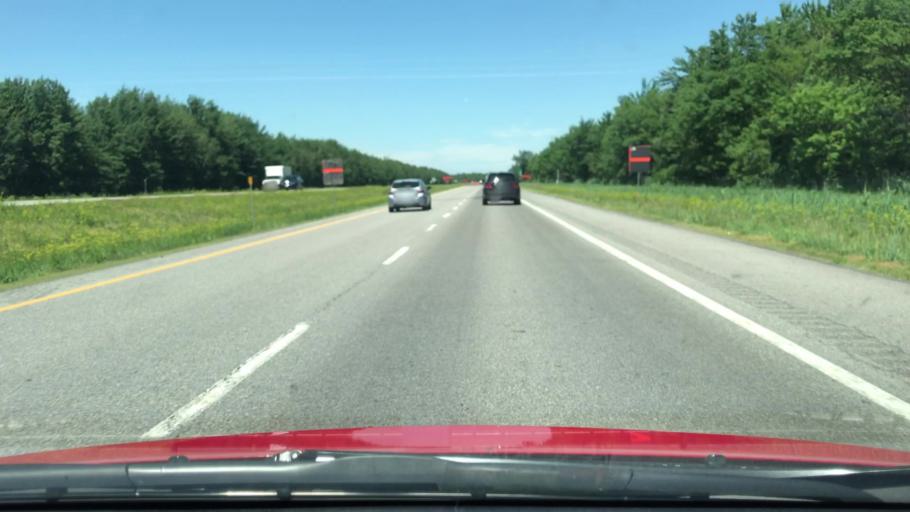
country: CA
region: Quebec
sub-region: Monteregie
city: Napierville
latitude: 45.1501
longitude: -73.4677
